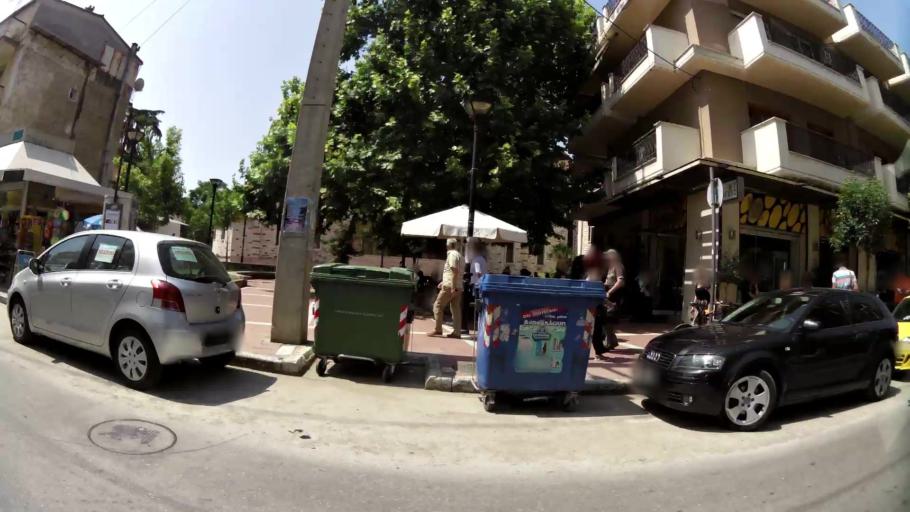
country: GR
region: Central Macedonia
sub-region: Nomos Thessalonikis
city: Evosmos
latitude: 40.6686
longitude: 22.9116
